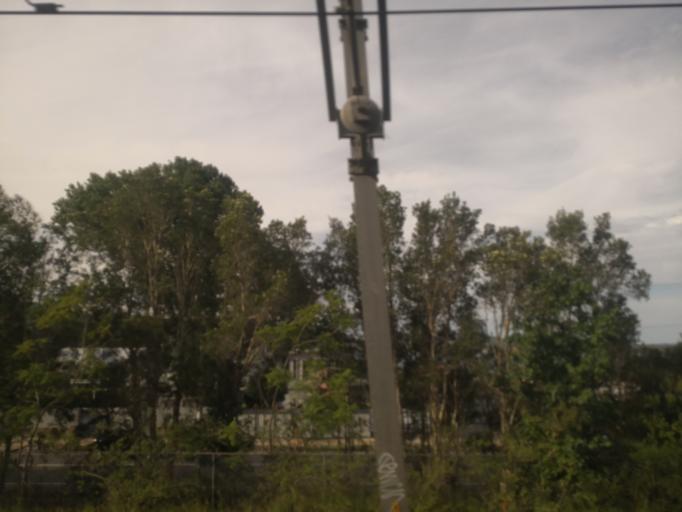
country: AU
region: New South Wales
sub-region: Gosford Shire
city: Point Clare
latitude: -33.4633
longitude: 151.3155
